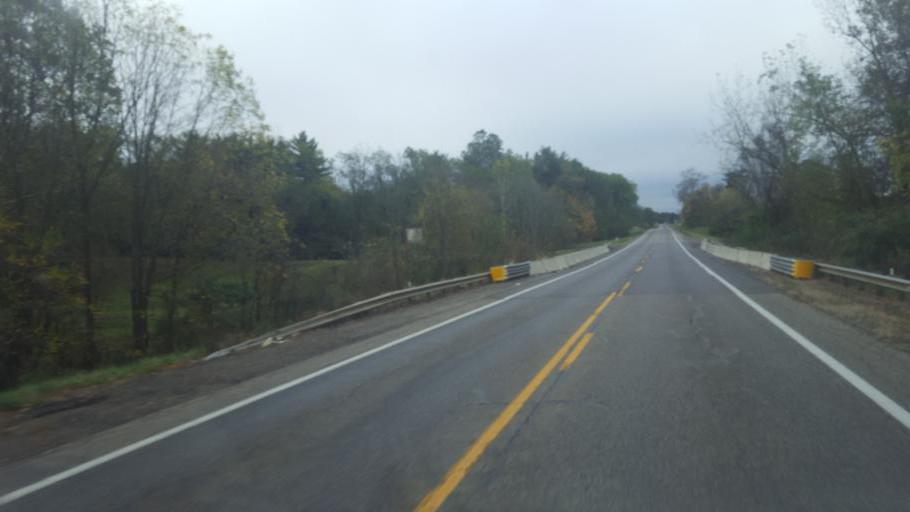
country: US
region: Ohio
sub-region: Morrow County
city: Mount Gilead
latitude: 40.4874
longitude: -82.6995
